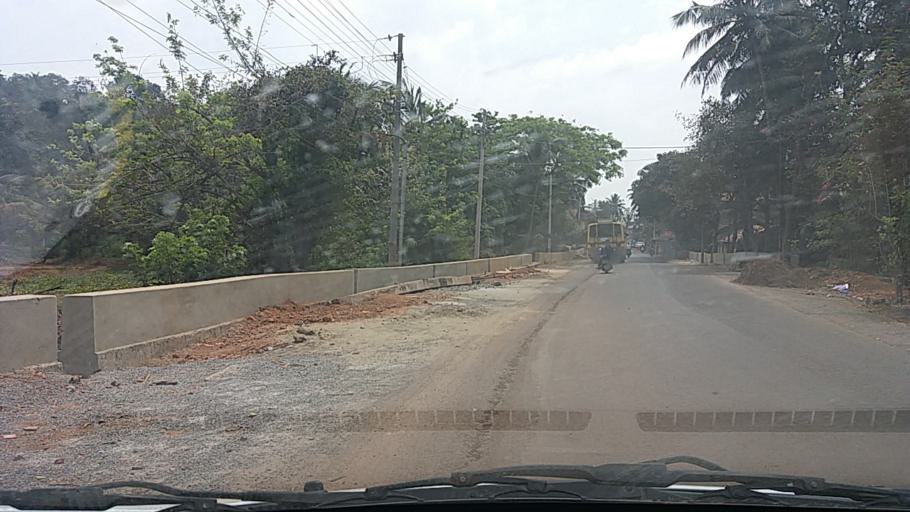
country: IN
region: Goa
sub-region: North Goa
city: Panaji
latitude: 15.5077
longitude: 73.8314
